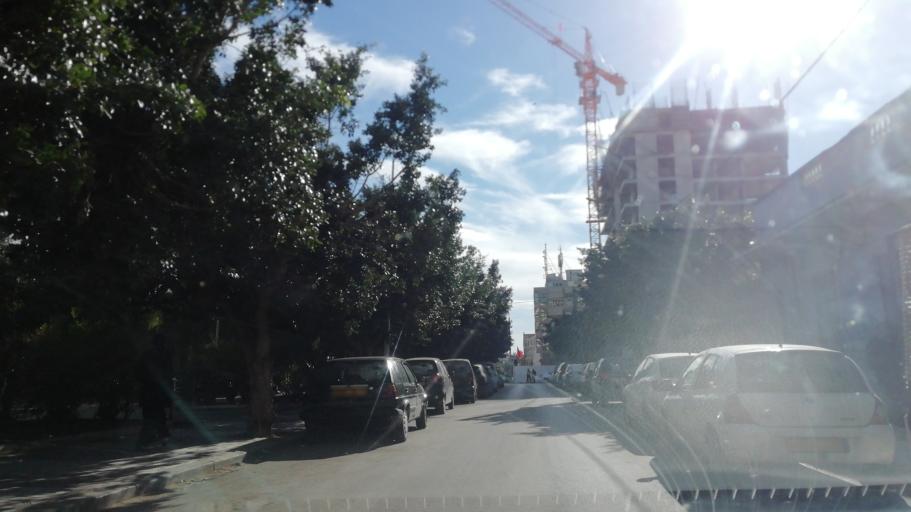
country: DZ
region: Oran
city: Oran
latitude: 35.6998
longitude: -0.6182
